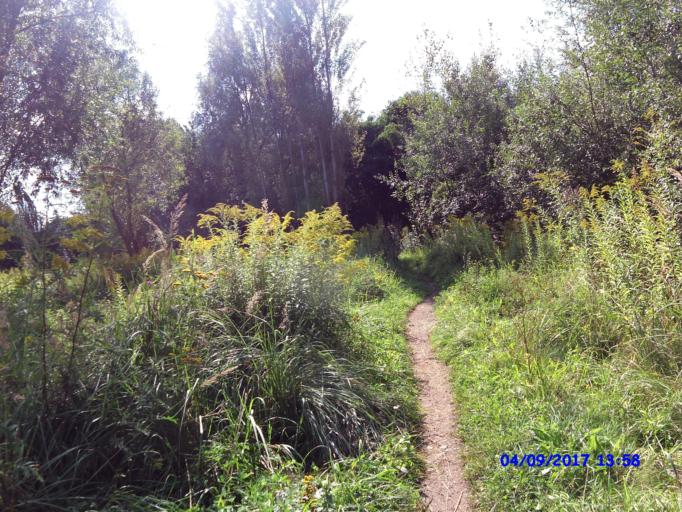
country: DE
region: Saxony
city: Taucha
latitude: 51.3522
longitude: 12.4675
